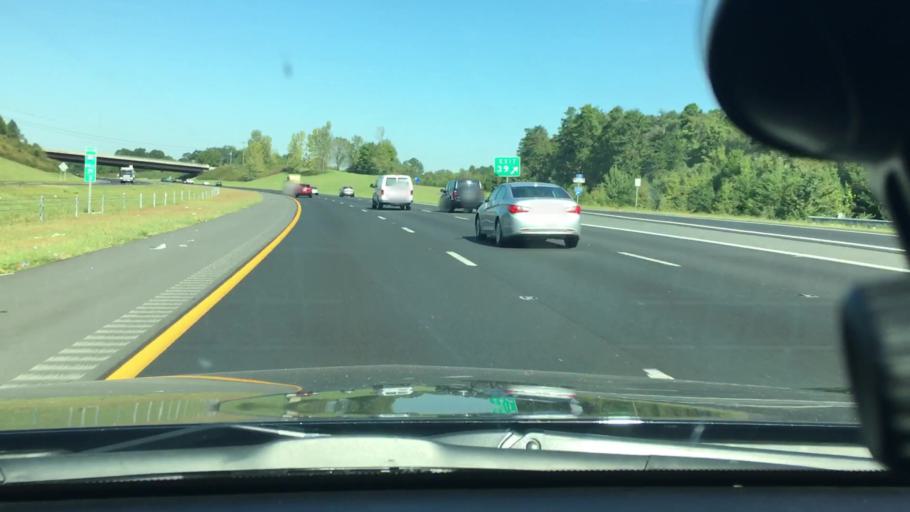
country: US
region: North Carolina
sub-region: Mecklenburg County
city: Mint Hill
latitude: 35.2502
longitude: -80.6513
